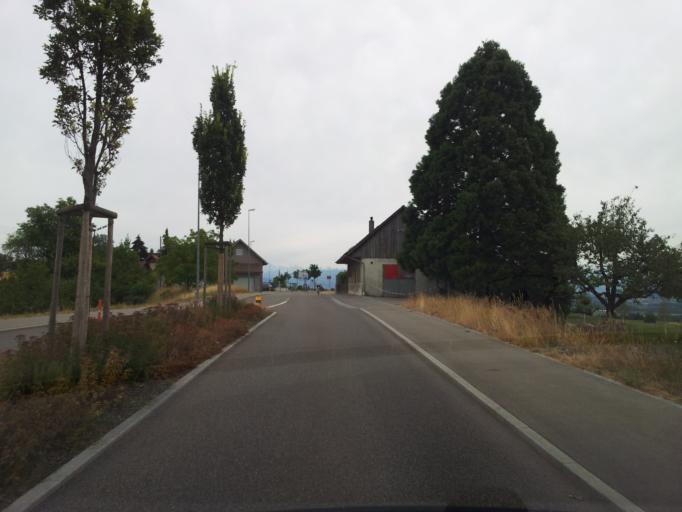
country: CH
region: Aargau
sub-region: Bezirk Bremgarten
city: Berikon
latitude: 47.3452
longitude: 8.3790
